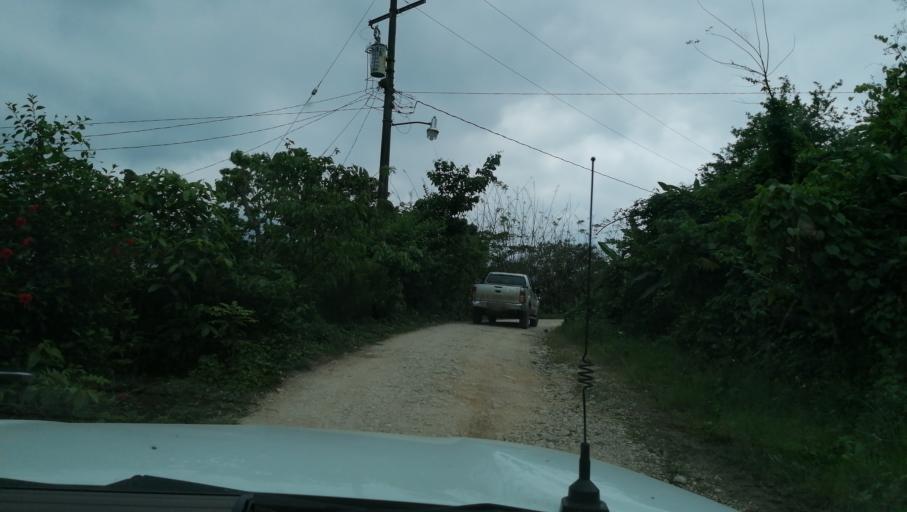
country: MX
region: Chiapas
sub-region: Ocotepec
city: San Pablo Huacano
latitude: 17.2738
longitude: -93.2423
